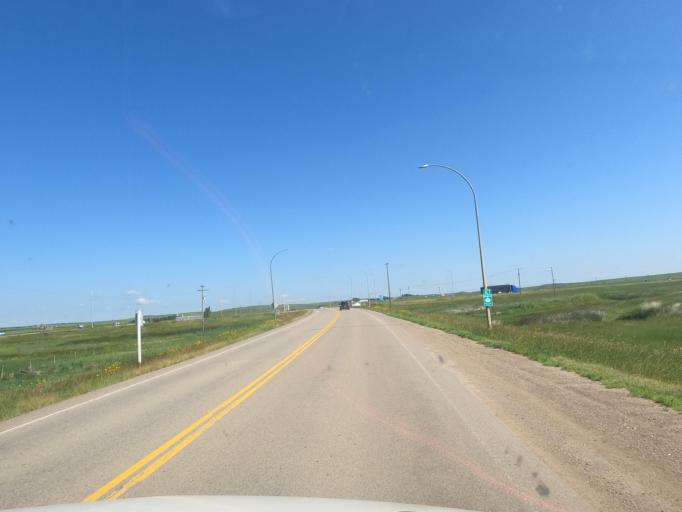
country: CA
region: Saskatchewan
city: Shaunavon
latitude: 50.0999
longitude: -108.4832
